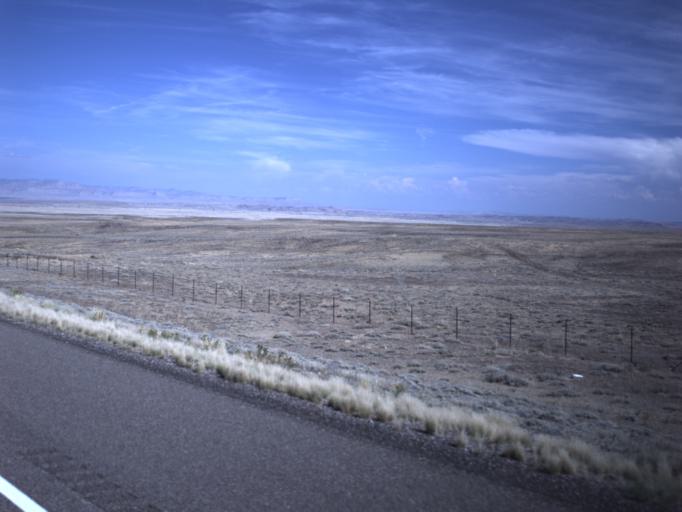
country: US
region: Utah
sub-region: Carbon County
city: East Carbon City
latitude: 38.9427
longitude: -110.3300
